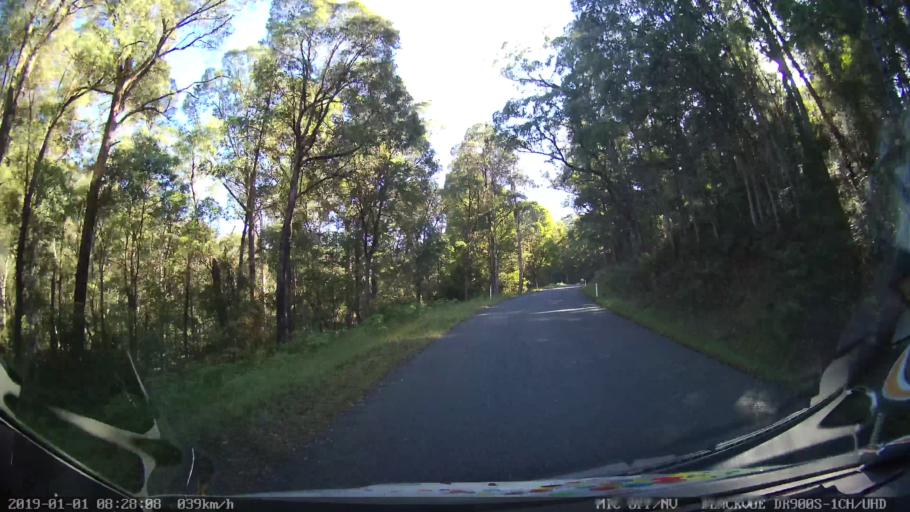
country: AU
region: New South Wales
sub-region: Snowy River
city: Jindabyne
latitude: -36.3777
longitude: 148.1879
